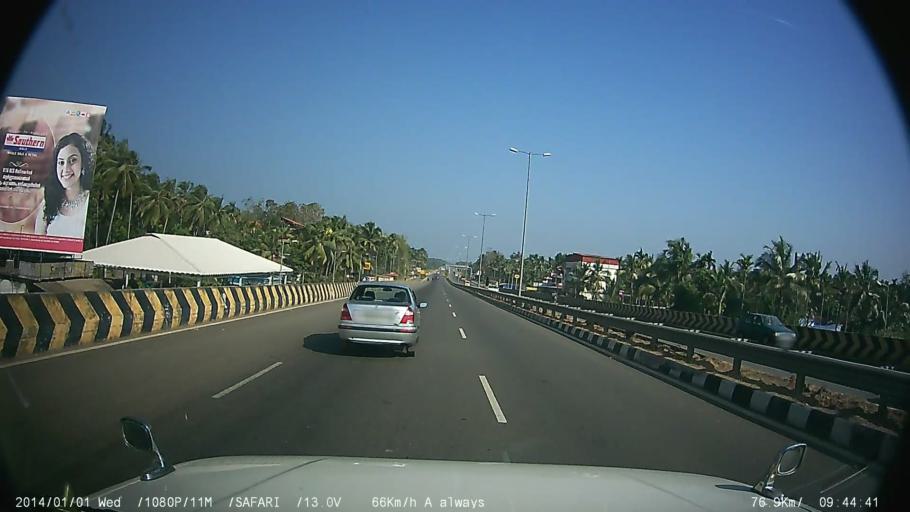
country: IN
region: Kerala
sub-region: Thrissur District
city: Trichur
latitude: 10.4508
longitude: 76.2581
